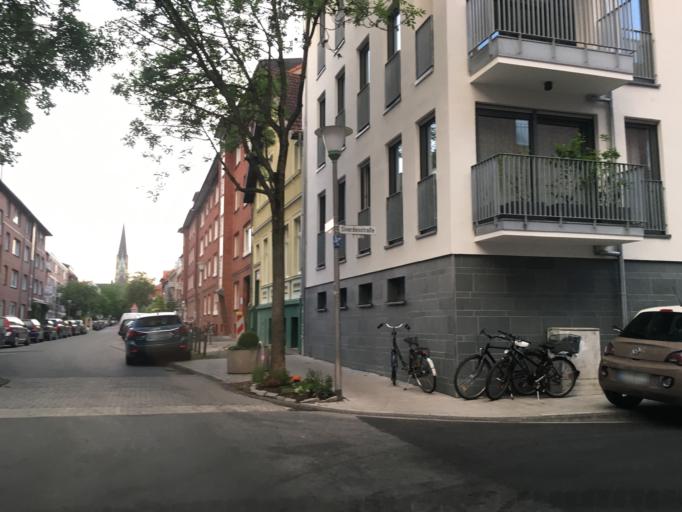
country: DE
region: North Rhine-Westphalia
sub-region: Regierungsbezirk Munster
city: Muenster
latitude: 51.9702
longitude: 7.6304
